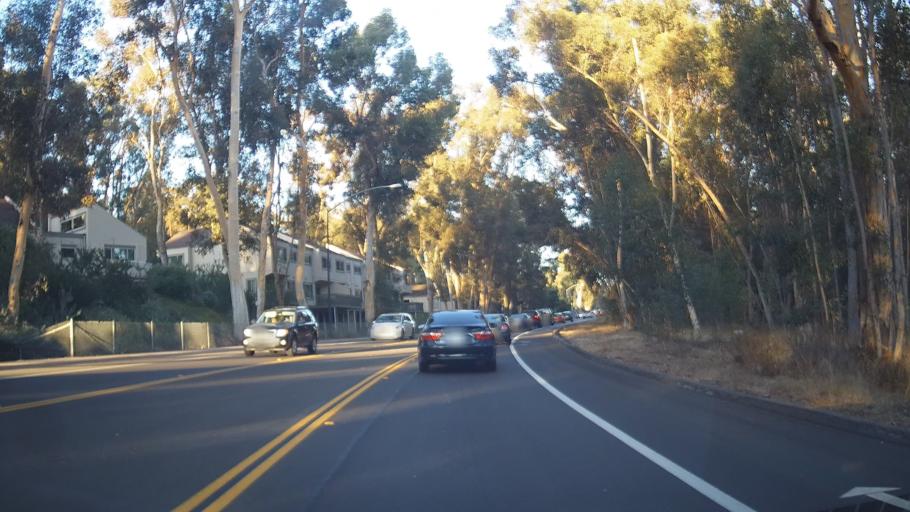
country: US
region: California
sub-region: San Diego County
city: Poway
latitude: 32.8958
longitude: -117.1073
